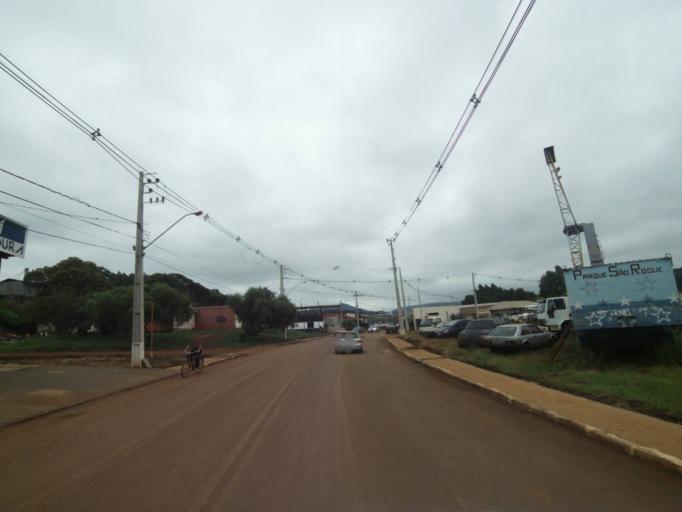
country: BR
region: Parana
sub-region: Pitanga
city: Pitanga
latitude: -24.9317
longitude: -51.8736
